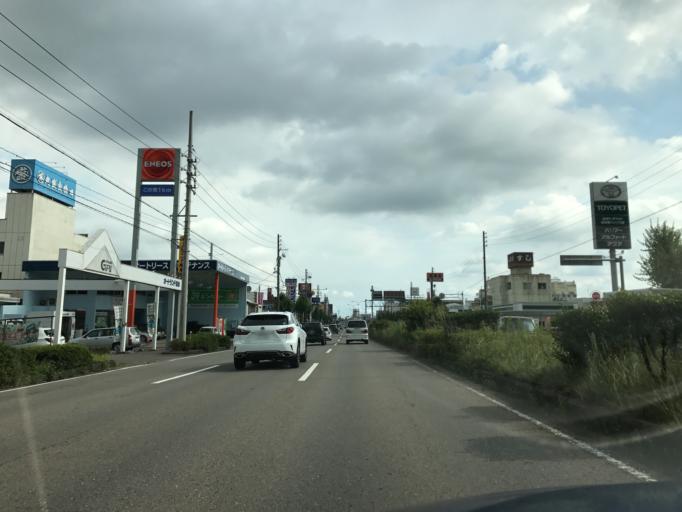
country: JP
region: Gifu
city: Gifu-shi
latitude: 35.4102
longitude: 136.7850
